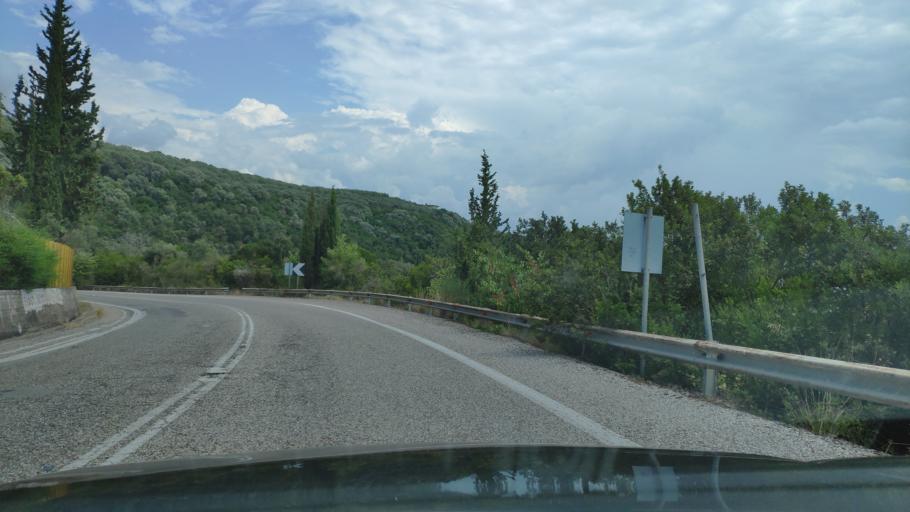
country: GR
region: West Greece
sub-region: Nomos Aitolias kai Akarnanias
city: Menidi
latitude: 39.0063
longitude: 21.1446
